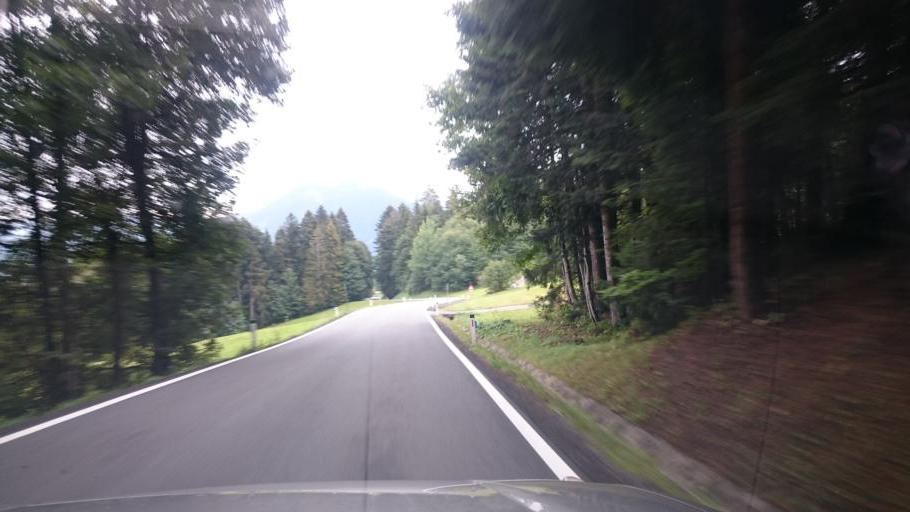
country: AT
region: Vorarlberg
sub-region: Politischer Bezirk Bregenz
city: Andelsbuch
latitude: 47.4154
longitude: 9.8261
